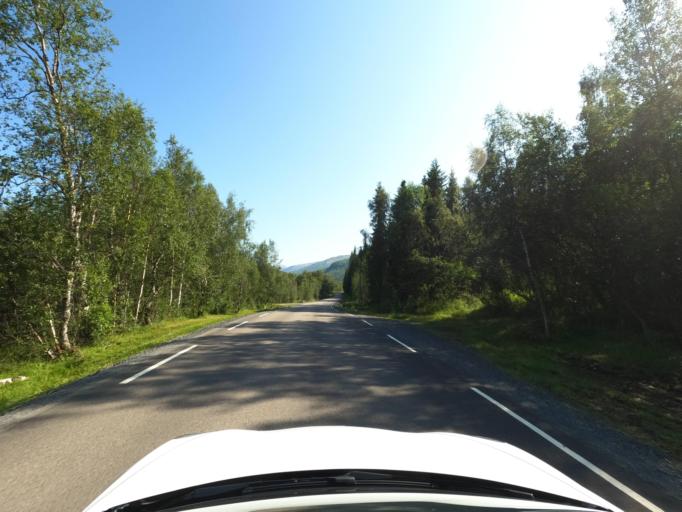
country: NO
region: Nordland
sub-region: Narvik
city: Narvik
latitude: 68.3925
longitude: 17.3366
